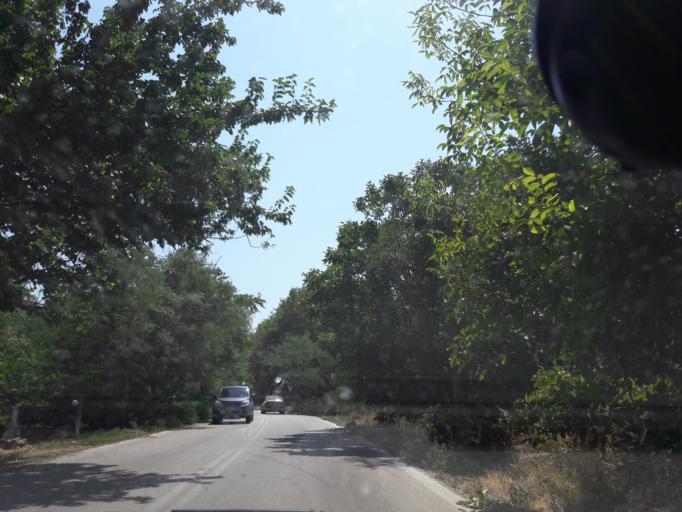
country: GR
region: North Aegean
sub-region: Nomos Lesvou
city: Myrina
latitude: 39.8686
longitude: 25.1548
